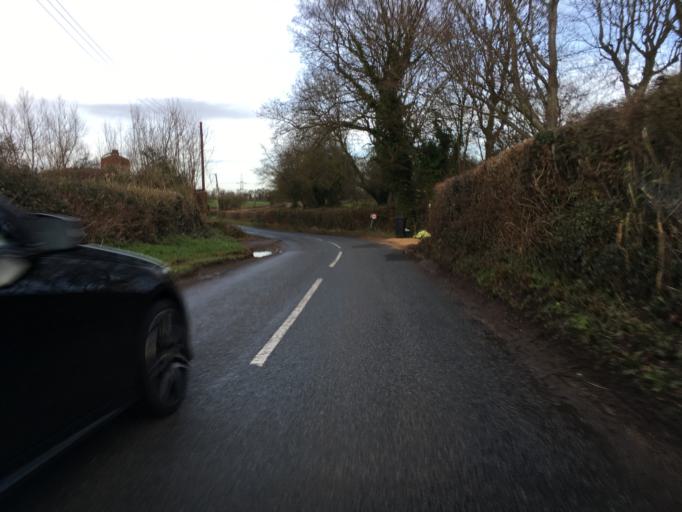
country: GB
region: England
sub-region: South Gloucestershire
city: Almondsbury
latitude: 51.5610
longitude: -2.5749
